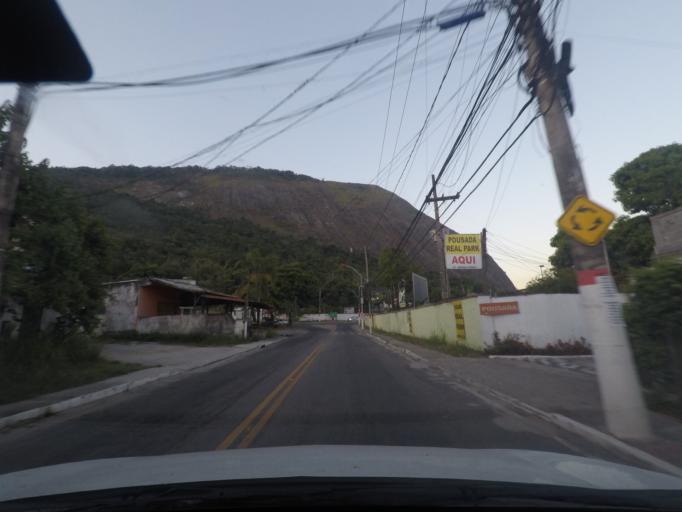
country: BR
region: Rio de Janeiro
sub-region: Marica
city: Marica
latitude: -22.9456
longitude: -42.9623
